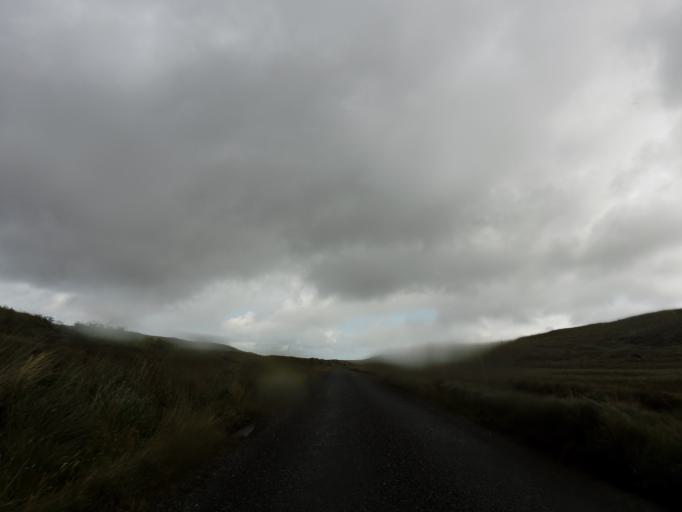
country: IE
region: Connaught
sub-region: County Galway
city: Oughterard
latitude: 53.3851
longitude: -9.3622
